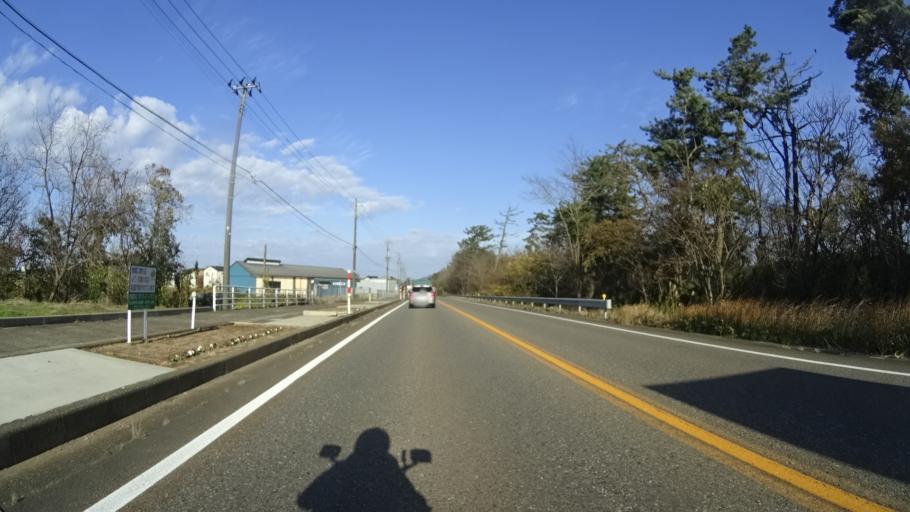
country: JP
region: Niigata
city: Joetsu
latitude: 37.2536
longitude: 138.3621
